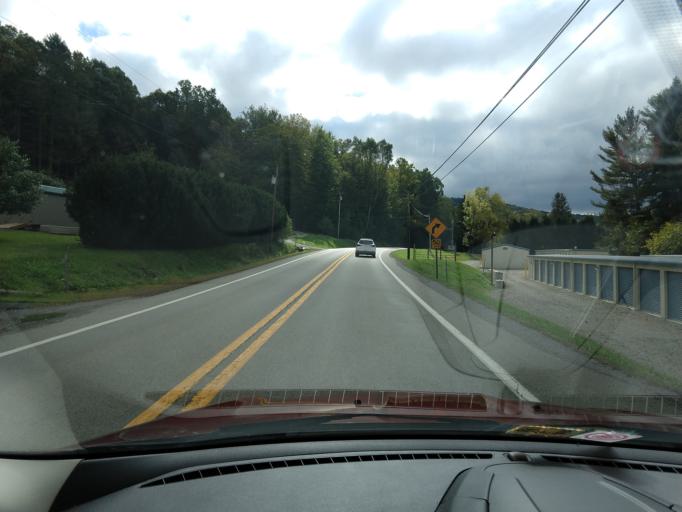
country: US
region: West Virginia
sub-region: Barbour County
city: Belington
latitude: 39.0008
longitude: -79.9362
